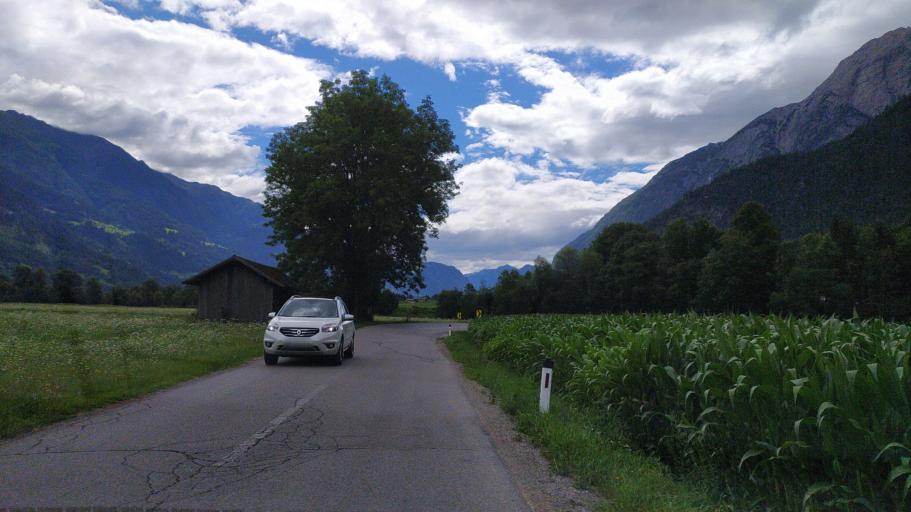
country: AT
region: Tyrol
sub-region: Politischer Bezirk Lienz
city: Lavant
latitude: 46.8021
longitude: 12.8350
